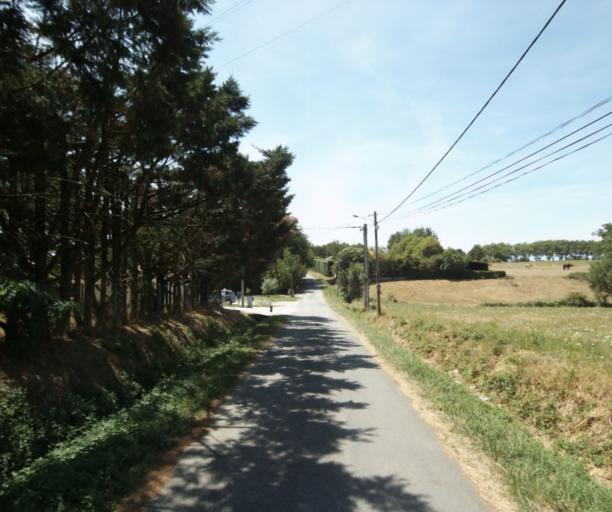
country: FR
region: Midi-Pyrenees
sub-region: Departement de la Haute-Garonne
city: Revel
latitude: 43.4913
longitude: 2.0179
